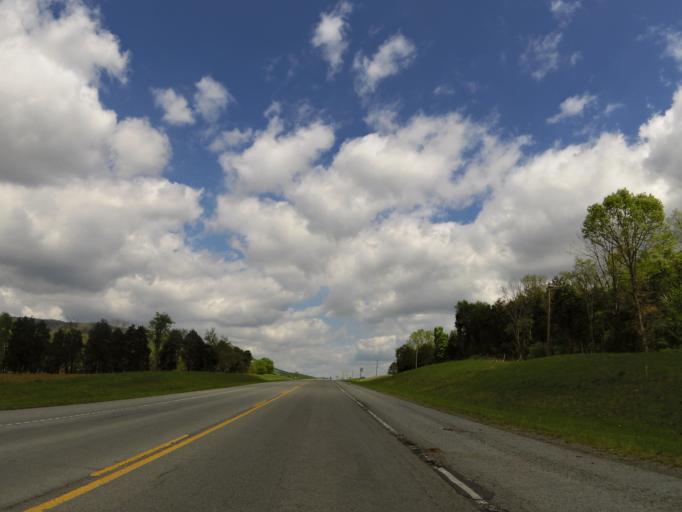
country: US
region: Tennessee
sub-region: Campbell County
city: Fincastle
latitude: 36.4501
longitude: -83.9252
